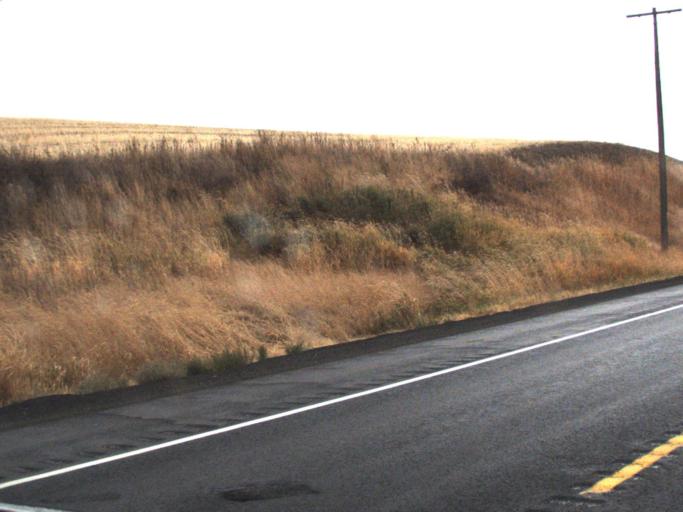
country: US
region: Washington
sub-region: Whitman County
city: Colfax
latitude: 46.7973
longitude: -117.3146
